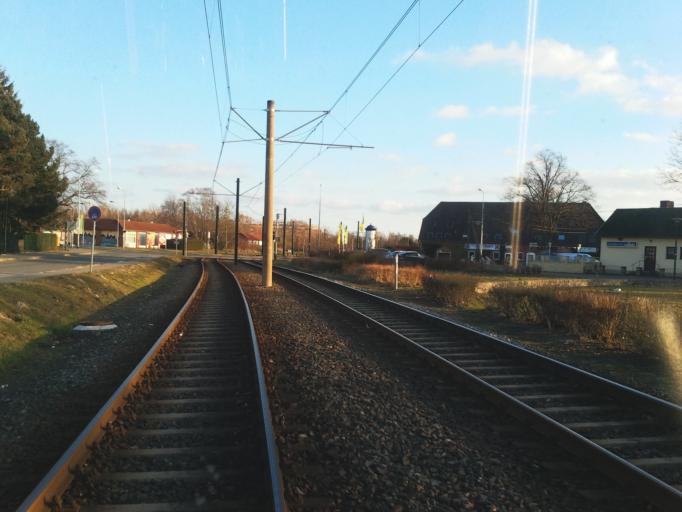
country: DE
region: Mecklenburg-Vorpommern
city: Dierkow-West
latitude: 54.1088
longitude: 12.1557
